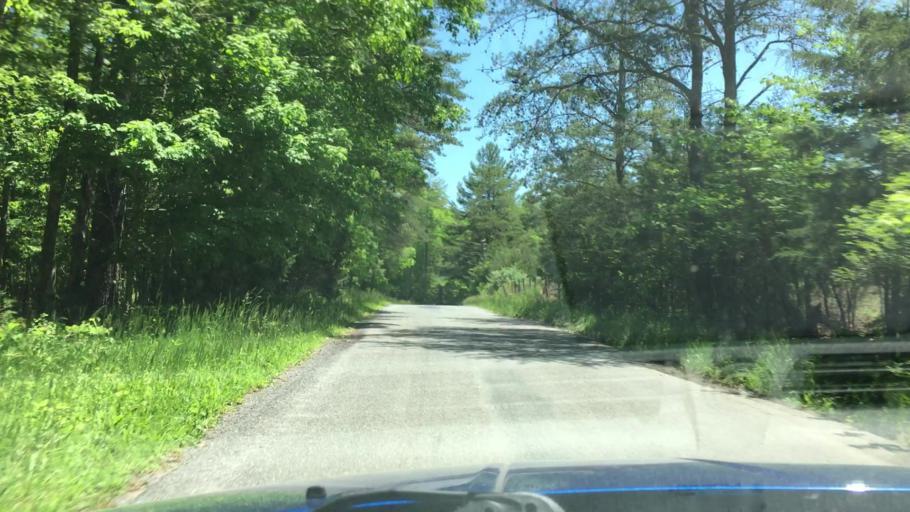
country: US
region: Virginia
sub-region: Bath County
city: Warm Springs
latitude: 38.0784
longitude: -79.5962
